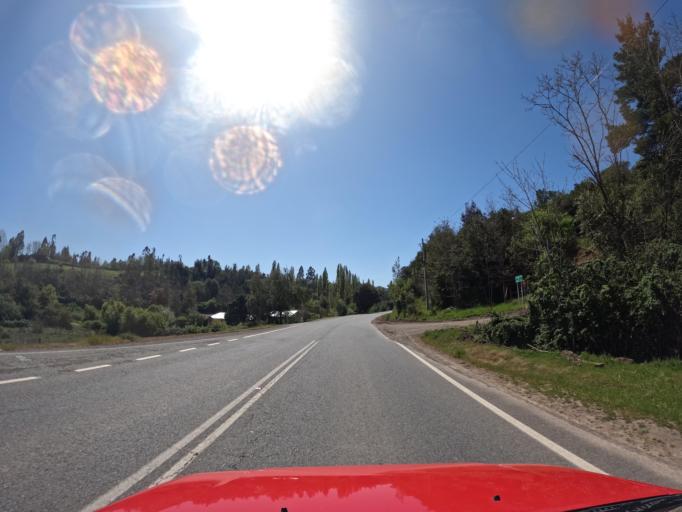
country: CL
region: Maule
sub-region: Provincia de Talca
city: San Clemente
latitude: -35.4614
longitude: -71.2695
